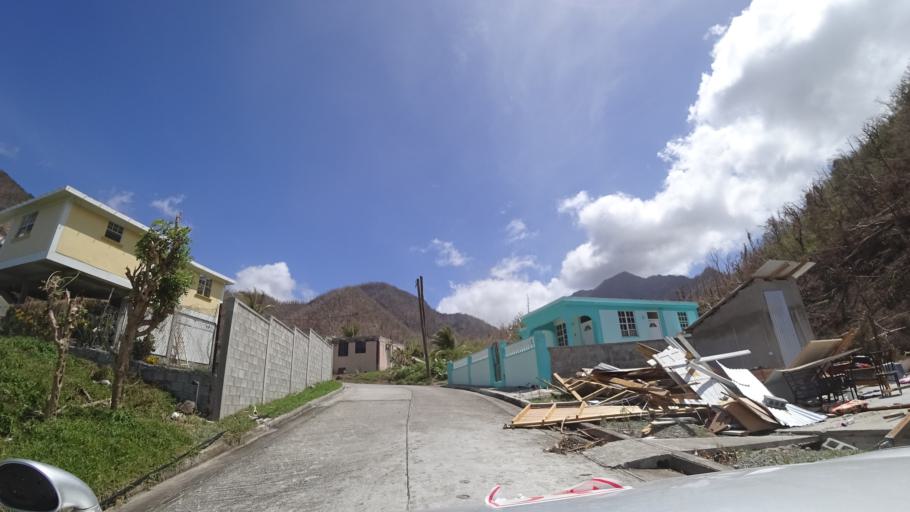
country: DM
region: Saint Luke
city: Pointe Michel
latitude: 15.2594
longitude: -61.3735
